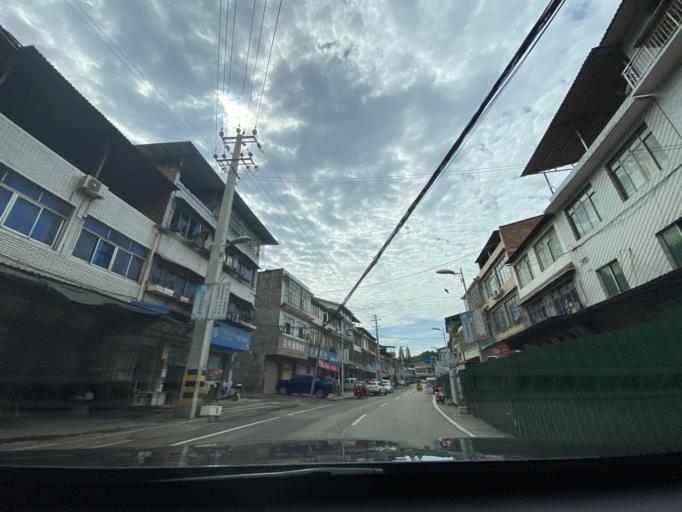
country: CN
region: Sichuan
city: Jiancheng
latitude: 30.4872
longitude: 104.6289
